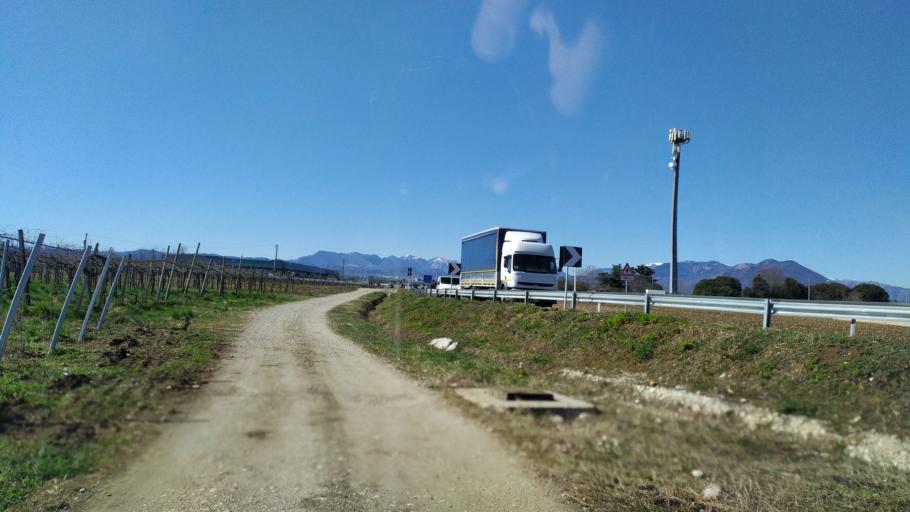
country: IT
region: Veneto
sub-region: Provincia di Vicenza
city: Breganze
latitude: 45.6938
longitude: 11.5681
